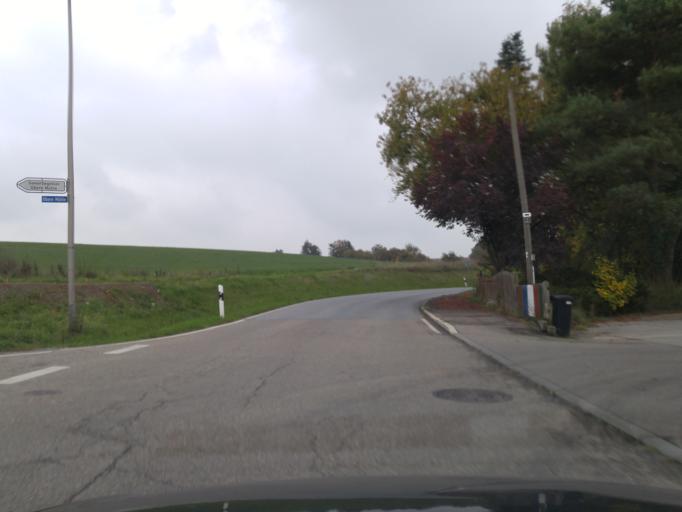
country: DE
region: Baden-Wuerttemberg
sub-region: Regierungsbezirk Stuttgart
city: Bad Rappenau
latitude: 49.2101
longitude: 9.0927
